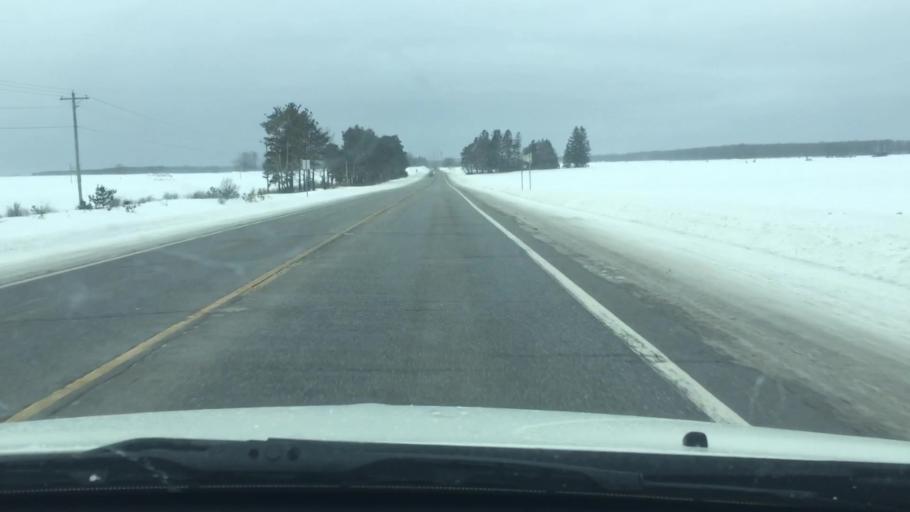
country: US
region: Michigan
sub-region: Otsego County
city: Gaylord
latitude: 45.0664
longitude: -84.8717
